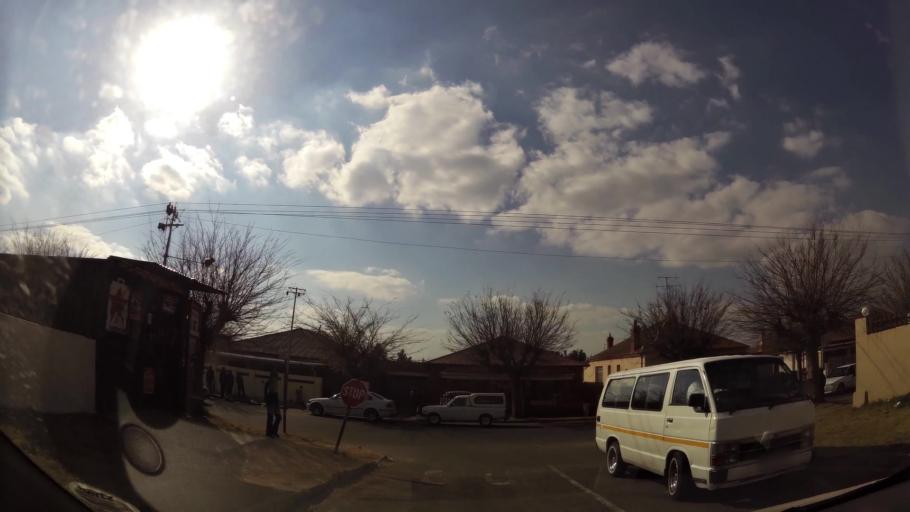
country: ZA
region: Gauteng
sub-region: West Rand District Municipality
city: Krugersdorp
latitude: -26.1072
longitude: 27.7731
